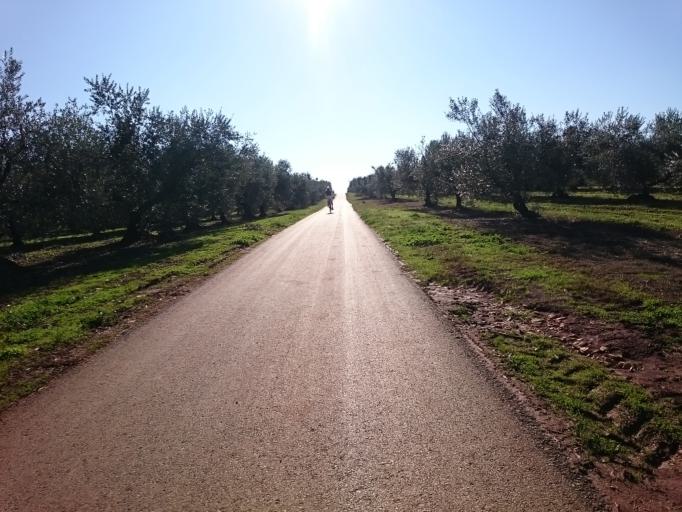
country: HR
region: Istarska
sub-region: Grad Porec
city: Porec
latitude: 45.2632
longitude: 13.5843
